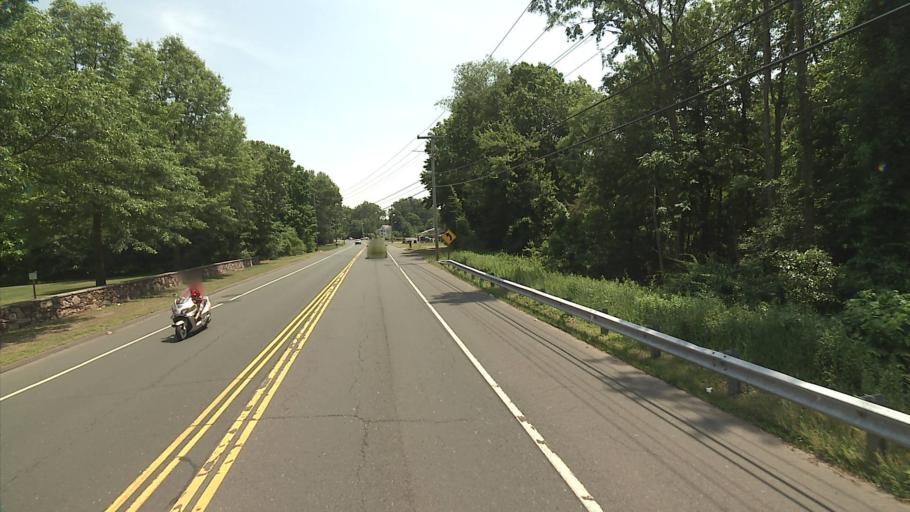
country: US
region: Connecticut
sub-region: Hartford County
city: East Hartford
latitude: 41.7657
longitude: -72.5859
